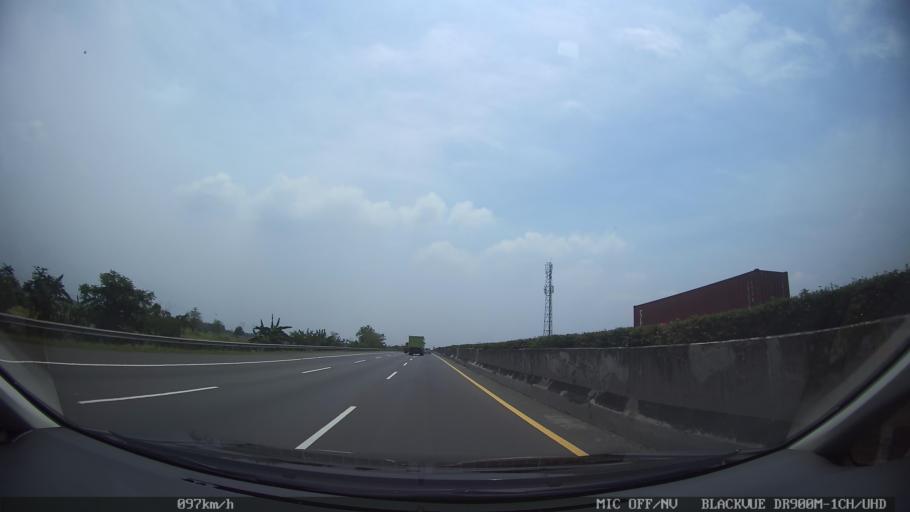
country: ID
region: West Java
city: Kresek
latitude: -6.1769
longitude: 106.3777
